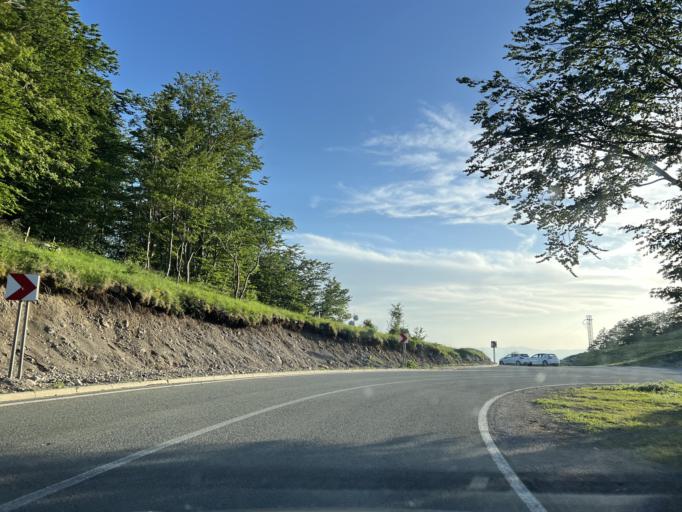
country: HR
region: Primorsko-Goranska
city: Podhum
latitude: 45.4110
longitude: 14.5587
